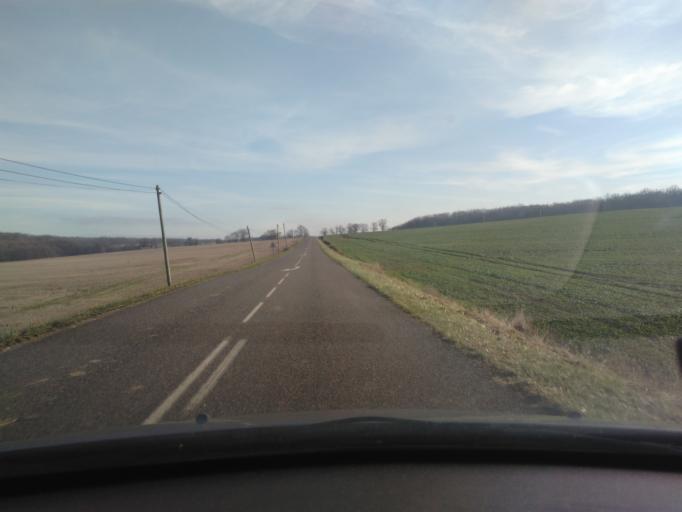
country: FR
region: Bourgogne
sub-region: Departement de la Nievre
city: Saint-Parize-le-Chatel
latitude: 46.8136
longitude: 3.2577
